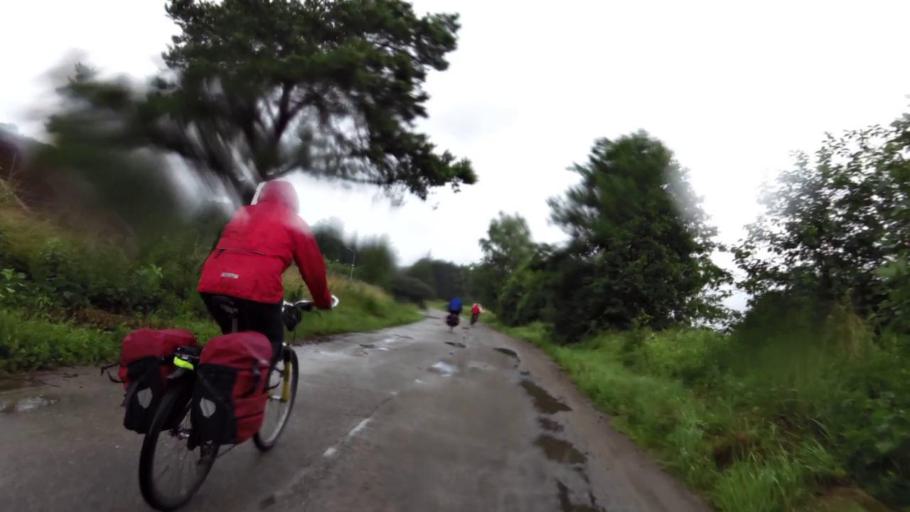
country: PL
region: West Pomeranian Voivodeship
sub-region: Powiat kolobrzeski
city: Ustronie Morskie
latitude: 54.2309
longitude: 15.8191
